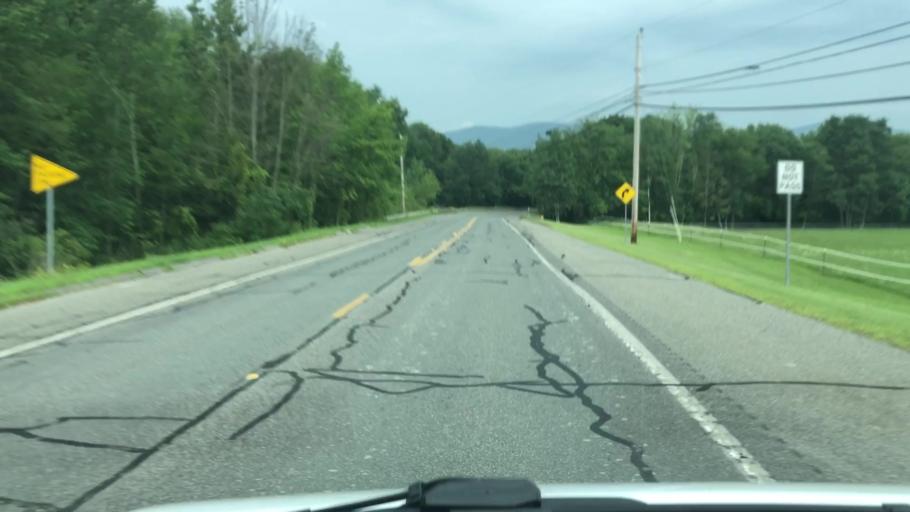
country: US
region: Massachusetts
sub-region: Berkshire County
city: Williamstown
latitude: 42.6428
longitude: -73.2319
